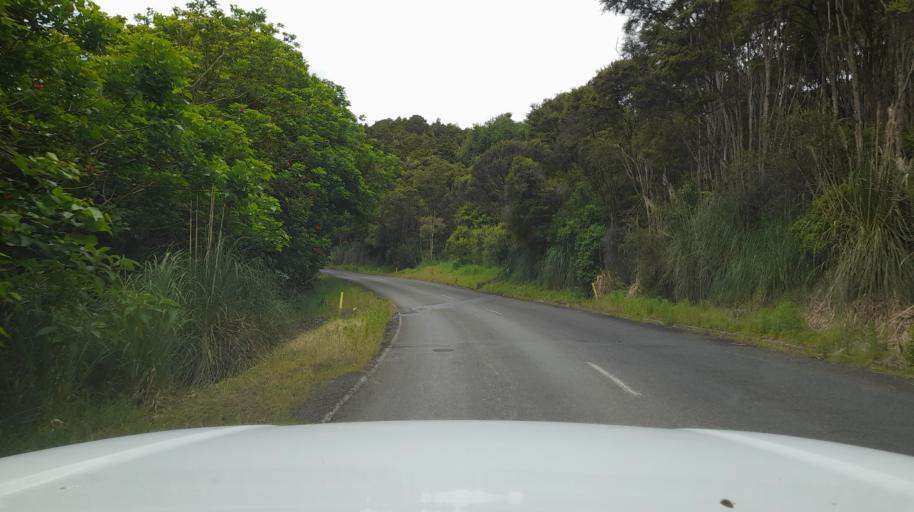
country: NZ
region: Northland
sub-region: Far North District
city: Kaitaia
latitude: -35.3606
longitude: 173.4578
